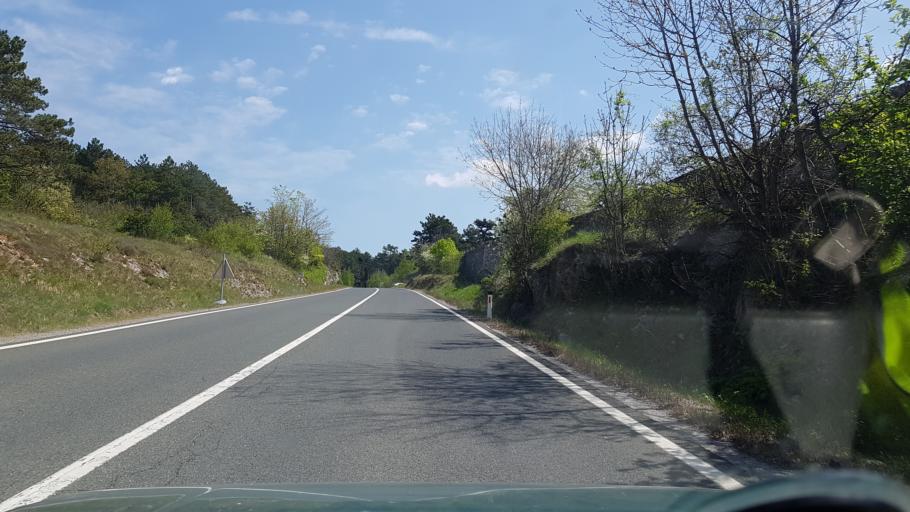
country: SI
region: Hrpelje-Kozina
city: Kozina
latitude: 45.6111
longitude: 13.9389
